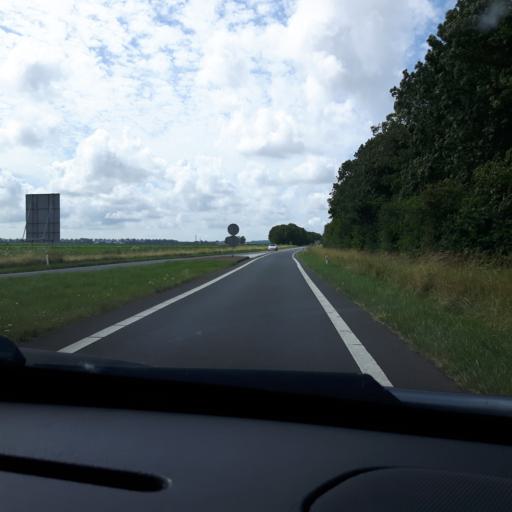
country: NL
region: Zeeland
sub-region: Gemeente Goes
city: Goes
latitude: 51.5695
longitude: 3.8449
